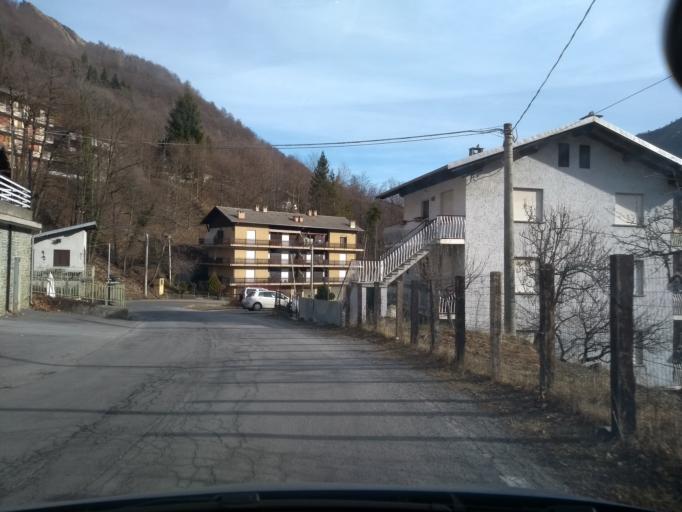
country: IT
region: Piedmont
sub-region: Provincia di Torino
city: Ala di Stura
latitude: 45.3146
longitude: 7.3090
